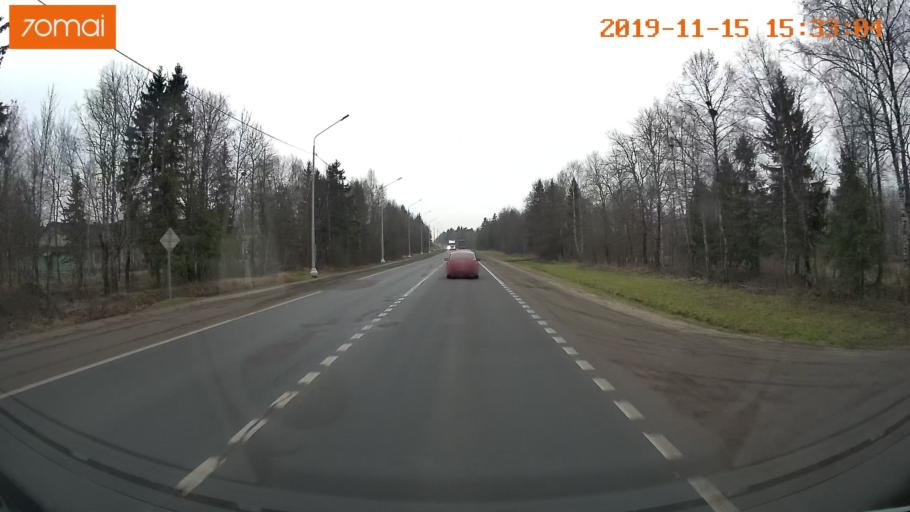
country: RU
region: Jaroslavl
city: Danilov
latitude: 58.0844
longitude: 40.0944
